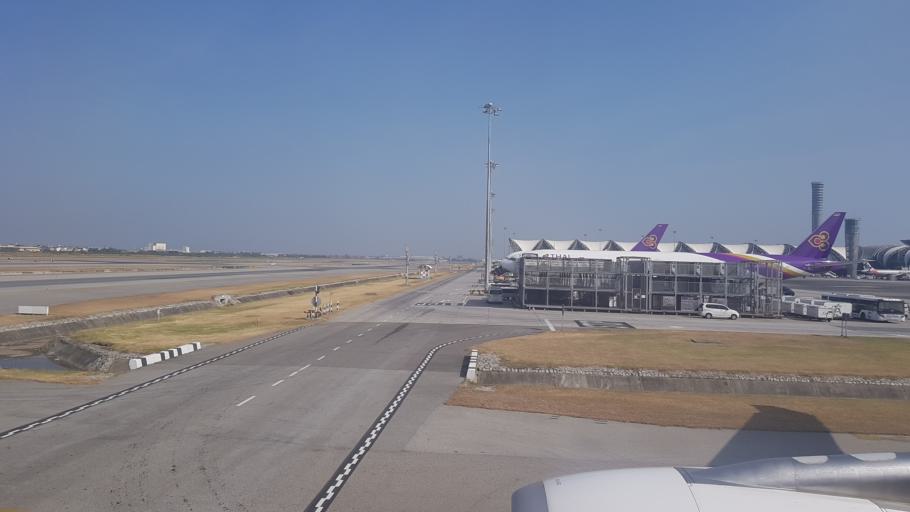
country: TH
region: Bangkok
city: Lat Krabang
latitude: 13.6879
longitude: 100.7427
